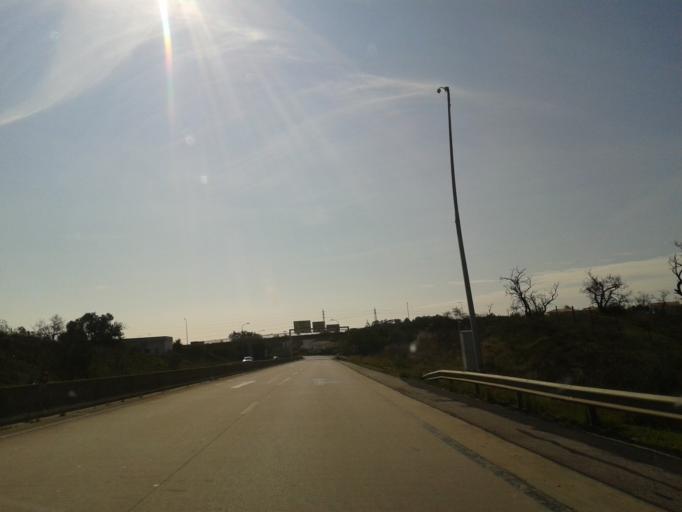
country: PT
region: Faro
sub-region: Faro
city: Santa Barbara de Nexe
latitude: 37.0788
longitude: -7.9786
